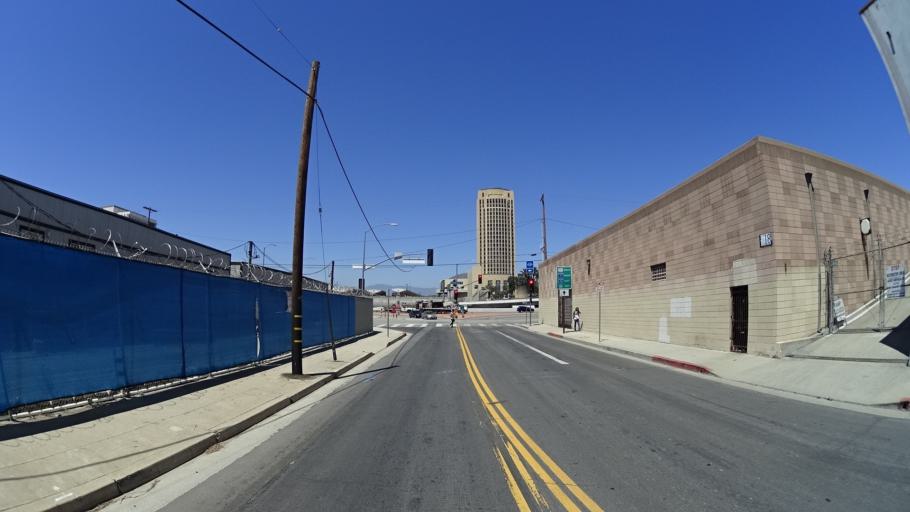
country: US
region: California
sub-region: Los Angeles County
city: Los Angeles
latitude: 34.0526
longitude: -118.2342
